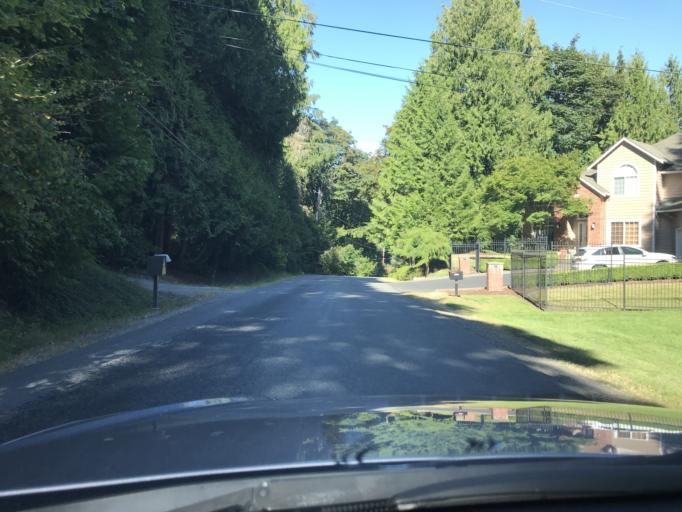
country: US
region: Washington
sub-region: King County
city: Maple Heights-Lake Desire
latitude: 47.4420
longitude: -122.0868
